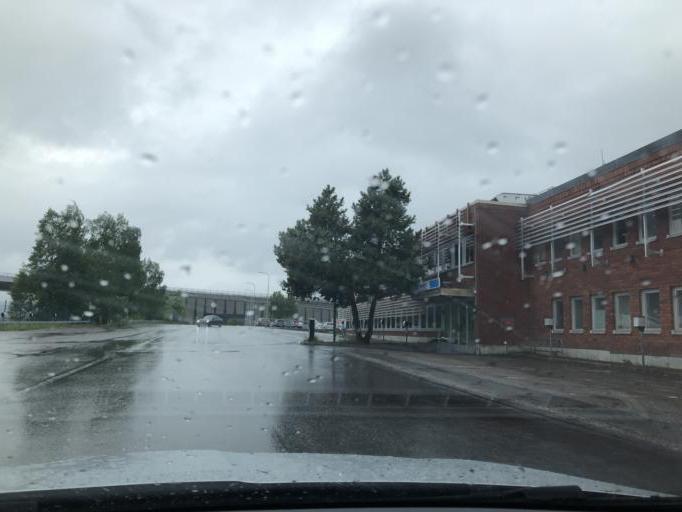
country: SE
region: Vaesternorrland
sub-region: Sundsvalls Kommun
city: Sundsvall
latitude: 62.3953
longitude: 17.3421
